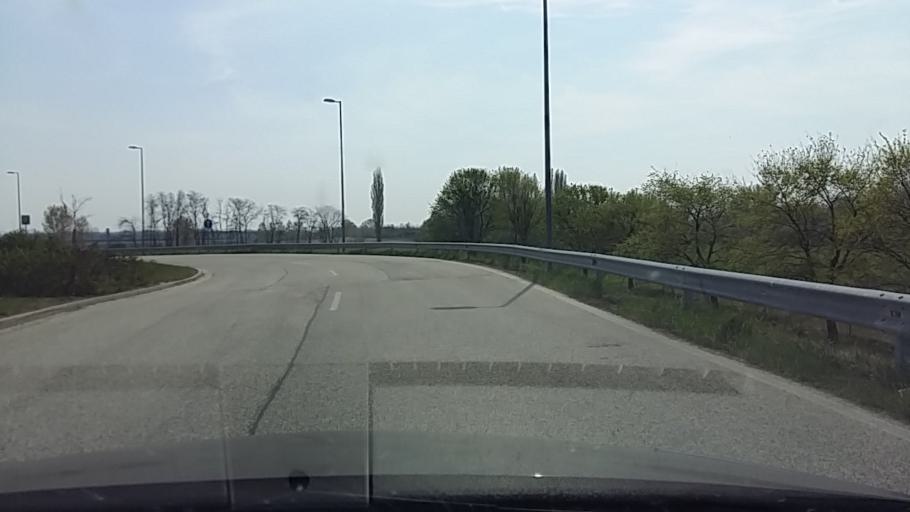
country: HU
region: Tolna
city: Paks
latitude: 46.6460
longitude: 18.8140
